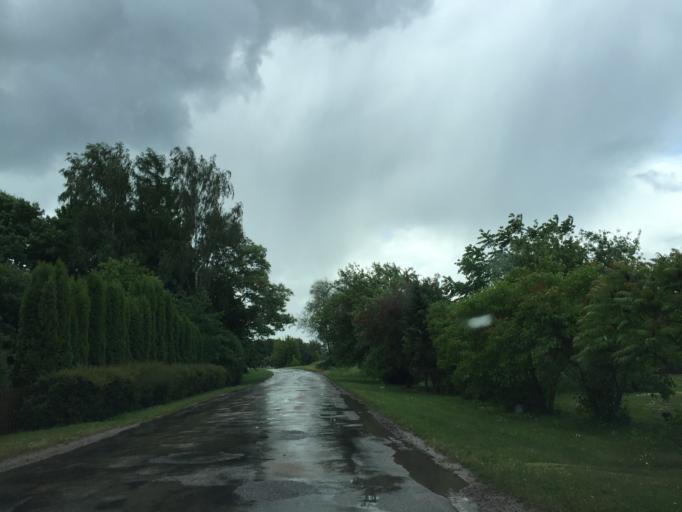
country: LV
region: Lecava
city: Iecava
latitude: 56.5961
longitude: 24.1882
